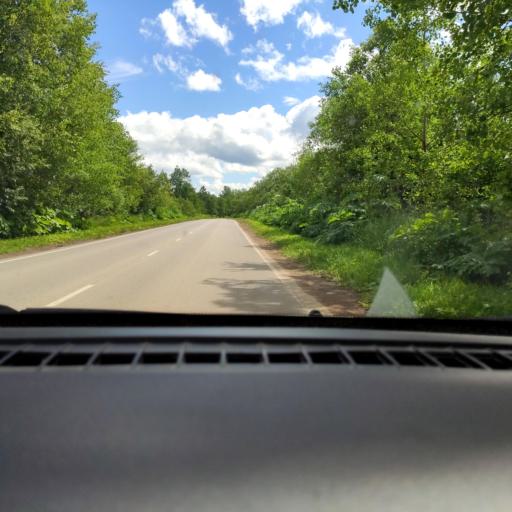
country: RU
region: Perm
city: Overyata
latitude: 58.1188
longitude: 55.8258
